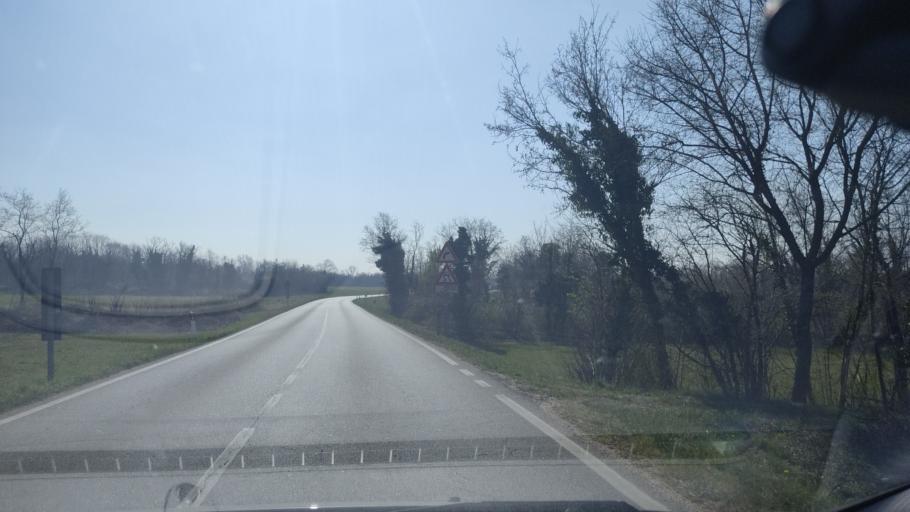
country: IT
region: Friuli Venezia Giulia
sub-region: Provincia di Pordenone
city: Budoia
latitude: 46.0350
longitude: 12.5490
